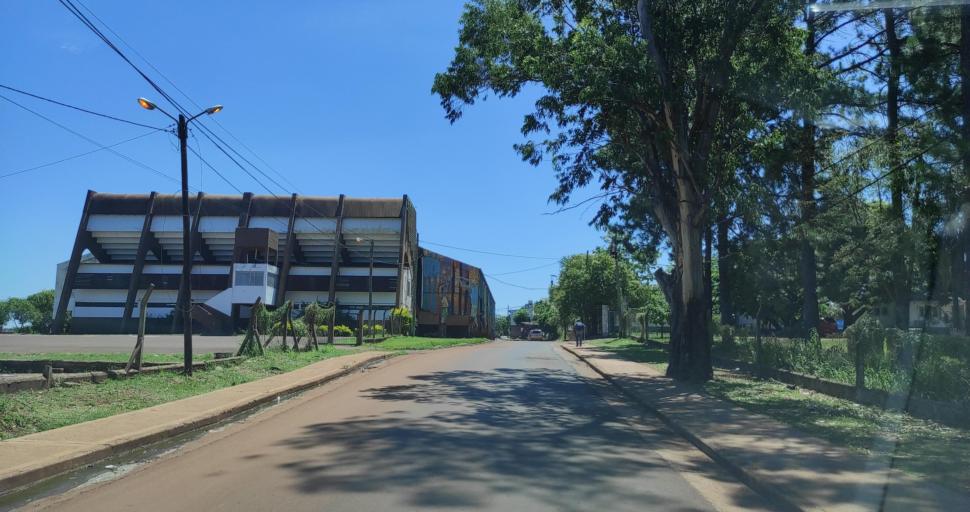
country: AR
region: Misiones
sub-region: Departamento de Capital
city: Posadas
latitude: -27.4168
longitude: -55.9028
